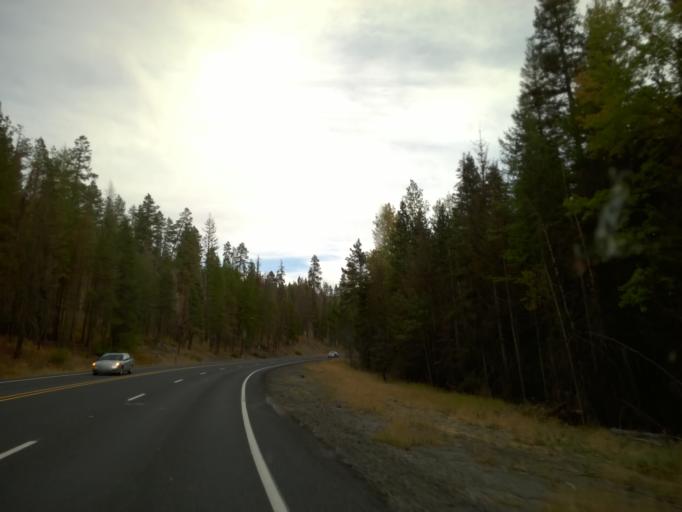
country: US
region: Washington
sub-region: Chelan County
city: Cashmere
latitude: 47.3464
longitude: -120.5666
